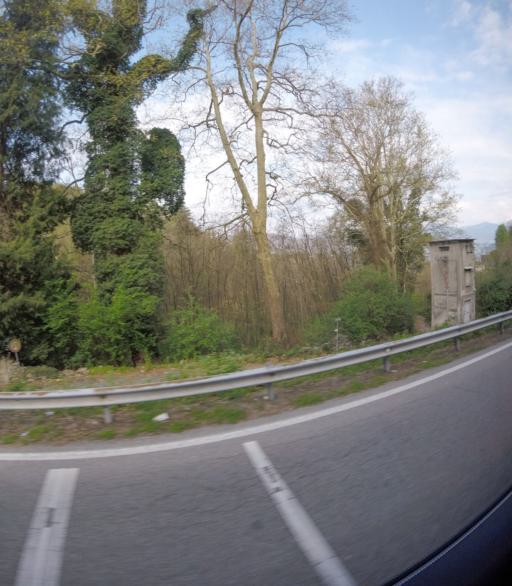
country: IT
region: Piedmont
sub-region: Provincia di Novara
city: Bolzano Novarese
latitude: 45.7602
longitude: 8.4300
